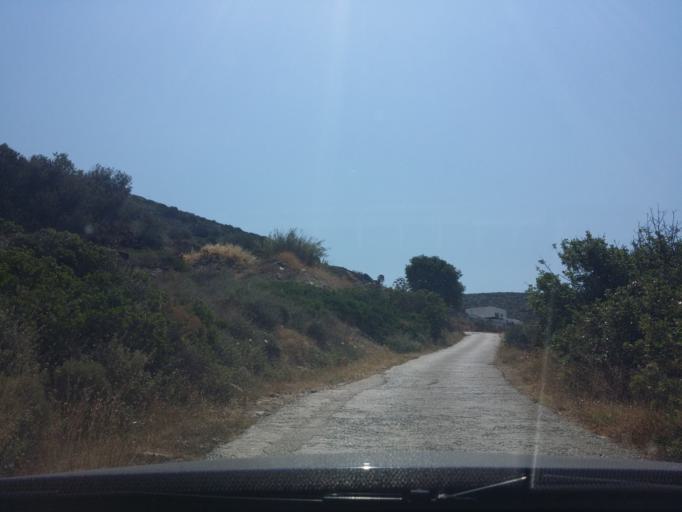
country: GR
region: South Aegean
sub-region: Nomos Kykladon
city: Paros
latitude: 37.0455
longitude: 25.1279
